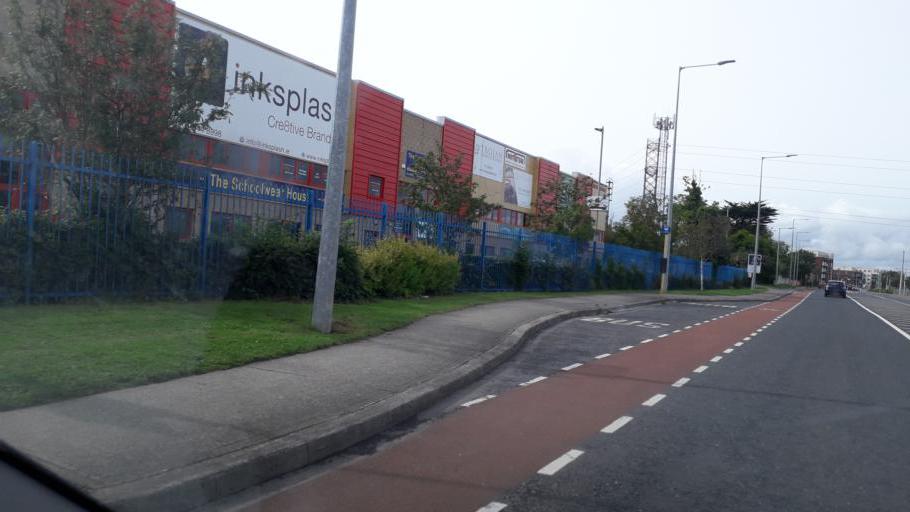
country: IE
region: Leinster
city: Foxrock
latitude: 53.2567
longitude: -6.1927
